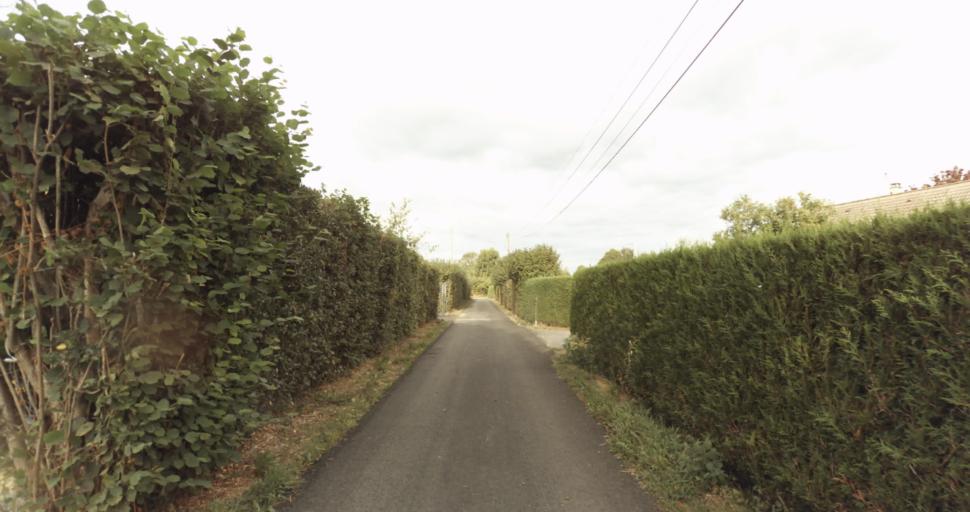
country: FR
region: Lower Normandy
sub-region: Departement de l'Orne
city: Vimoutiers
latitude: 48.9493
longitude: 0.2553
